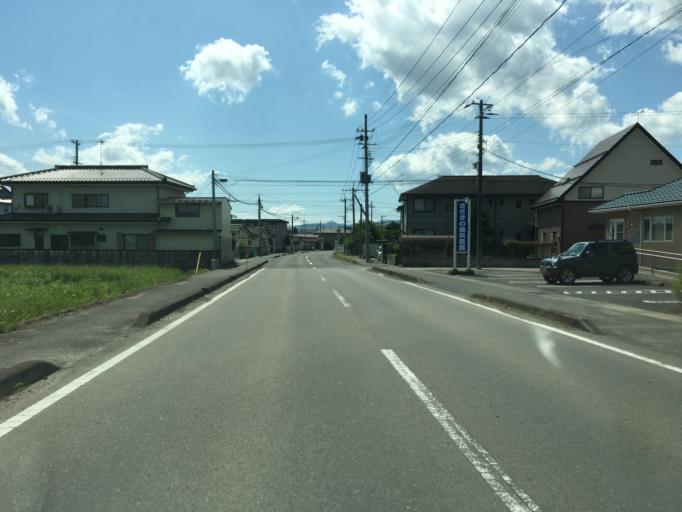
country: JP
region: Fukushima
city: Fukushima-shi
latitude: 37.7752
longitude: 140.4247
